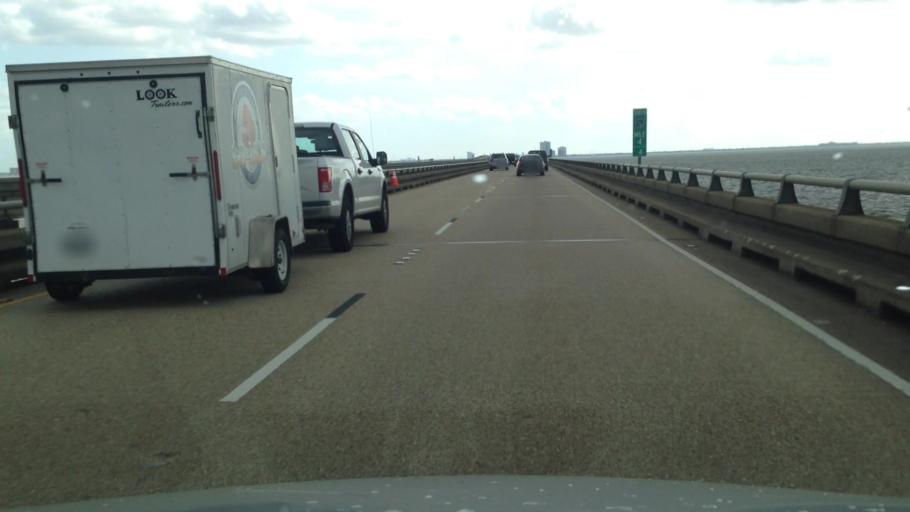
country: US
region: Louisiana
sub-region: Jefferson Parish
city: Metairie
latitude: 30.0852
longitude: -90.1430
